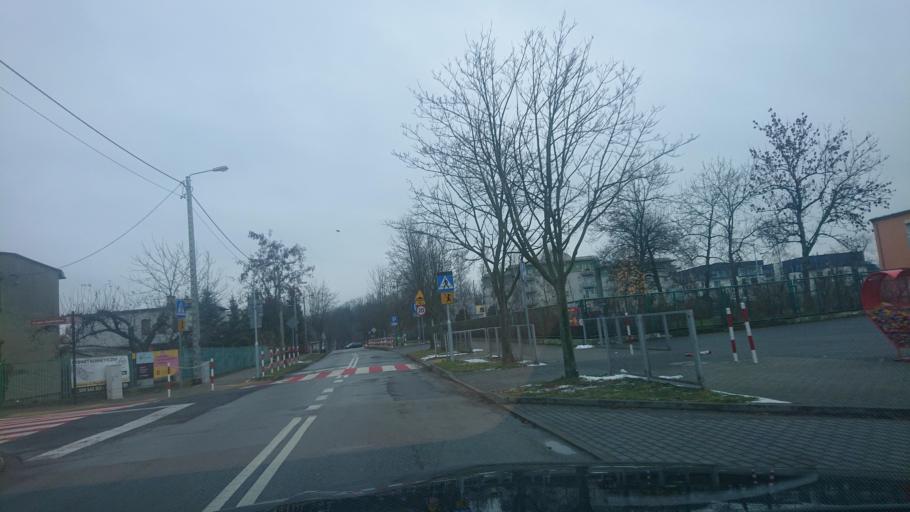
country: PL
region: Greater Poland Voivodeship
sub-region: Powiat gnieznienski
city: Gniezno
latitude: 52.5371
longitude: 17.5797
